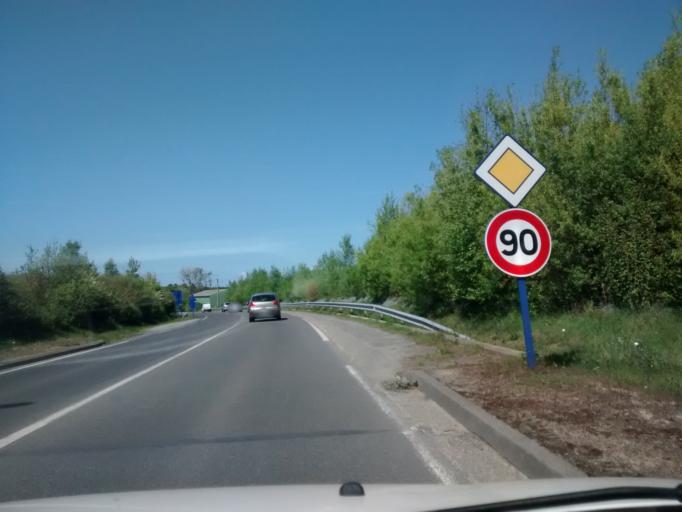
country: FR
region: Brittany
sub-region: Departement d'Ille-et-Vilaine
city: Pleurtuit
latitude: 48.5937
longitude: -2.0685
